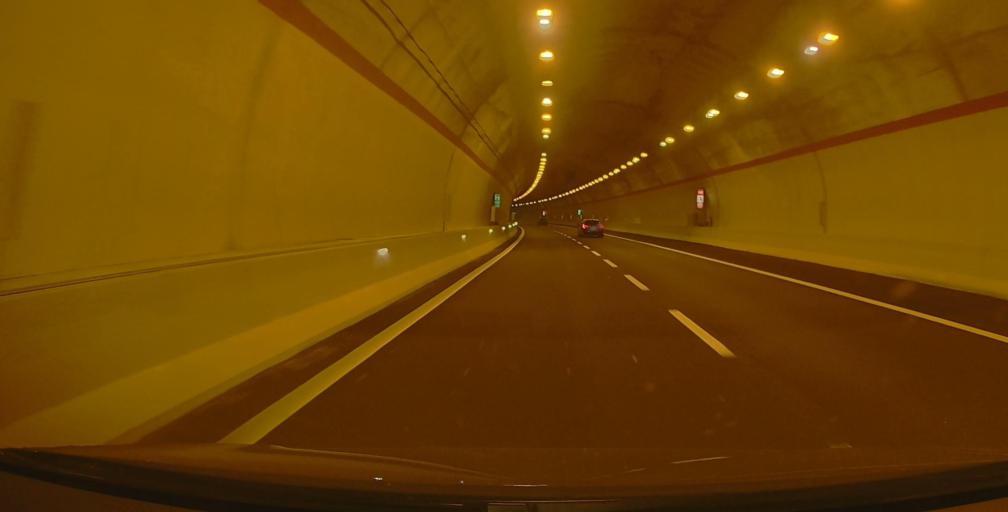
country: IT
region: Calabria
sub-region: Provincia di Cosenza
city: Laino Borgo
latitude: 39.9535
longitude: 15.9384
